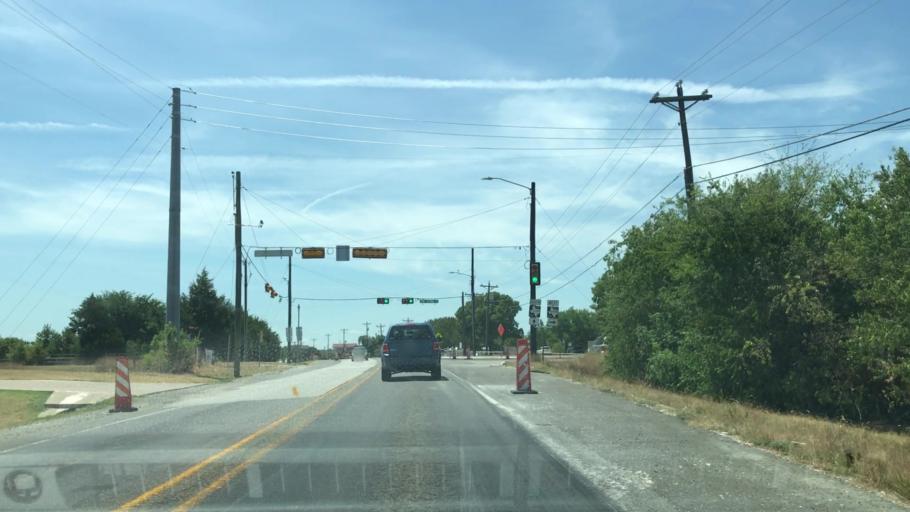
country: US
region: Texas
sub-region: Collin County
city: Fairview
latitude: 33.1292
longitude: -96.6113
